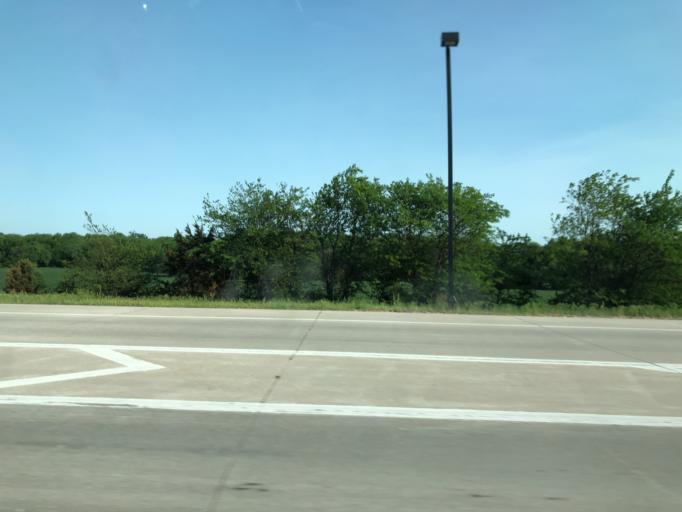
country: US
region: Nebraska
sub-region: Saunders County
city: Ashland
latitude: 41.0021
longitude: -96.3243
